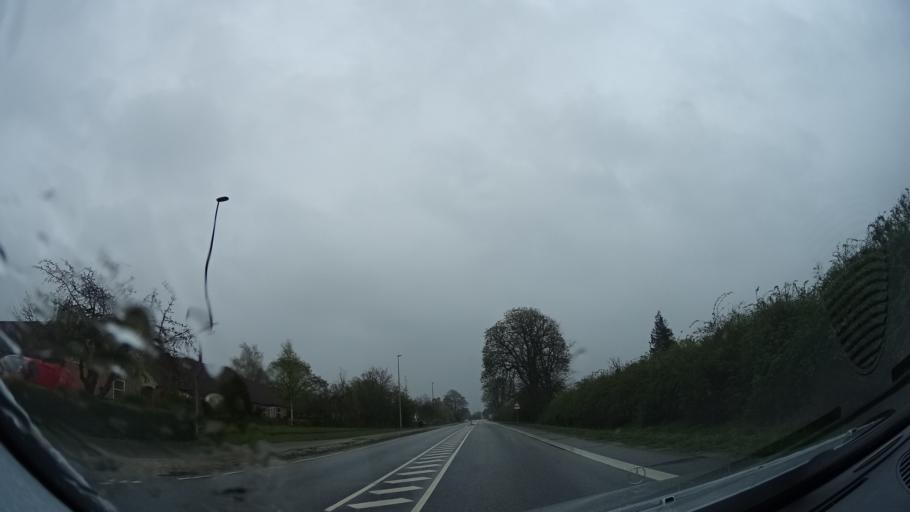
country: DK
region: Zealand
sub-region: Holbaek Kommune
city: Holbaek
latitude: 55.7134
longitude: 11.6228
